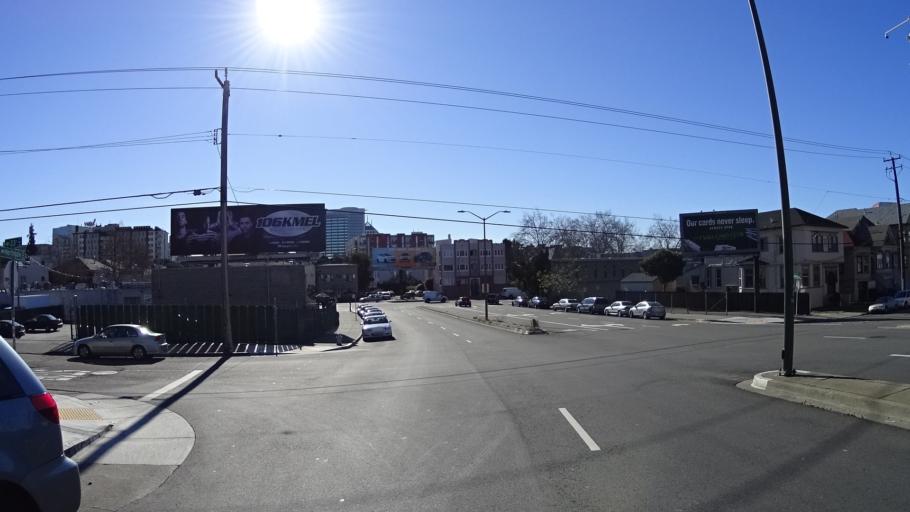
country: US
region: California
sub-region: Alameda County
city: Oakland
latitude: 37.8131
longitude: -122.2709
